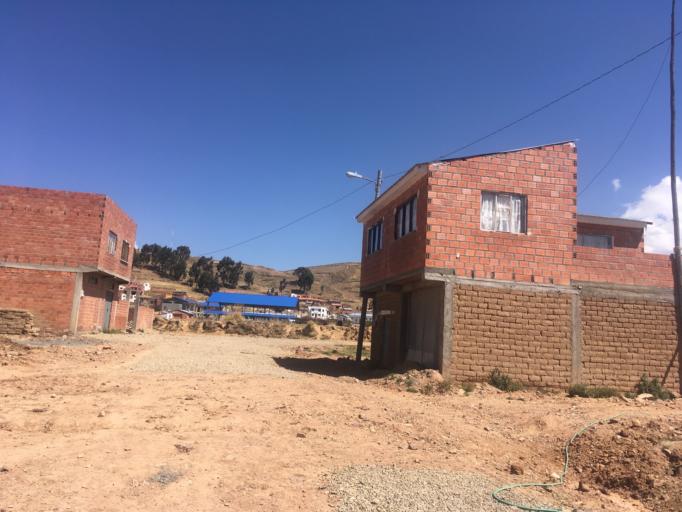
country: BO
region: La Paz
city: Huatajata
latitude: -16.1907
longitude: -68.7465
